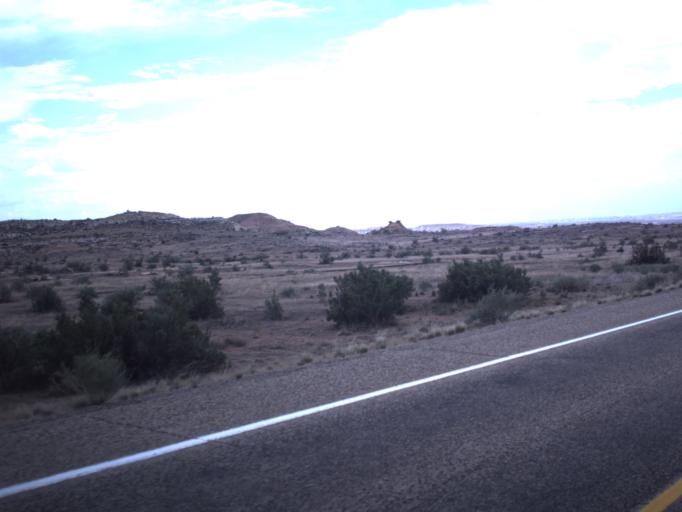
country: US
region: Utah
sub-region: Uintah County
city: Naples
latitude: 40.1314
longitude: -109.2639
